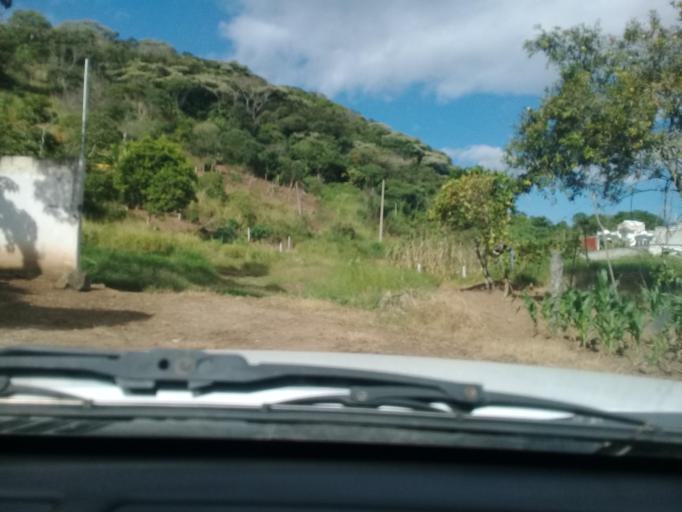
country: MX
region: Veracruz
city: El Castillo
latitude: 19.5442
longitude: -96.8798
